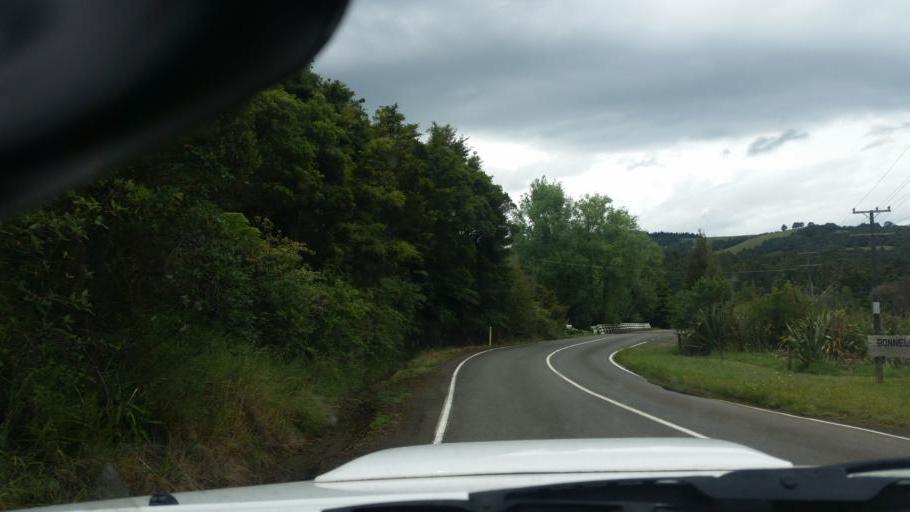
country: NZ
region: Northland
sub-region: Kaipara District
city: Dargaville
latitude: -35.7108
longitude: 173.6180
